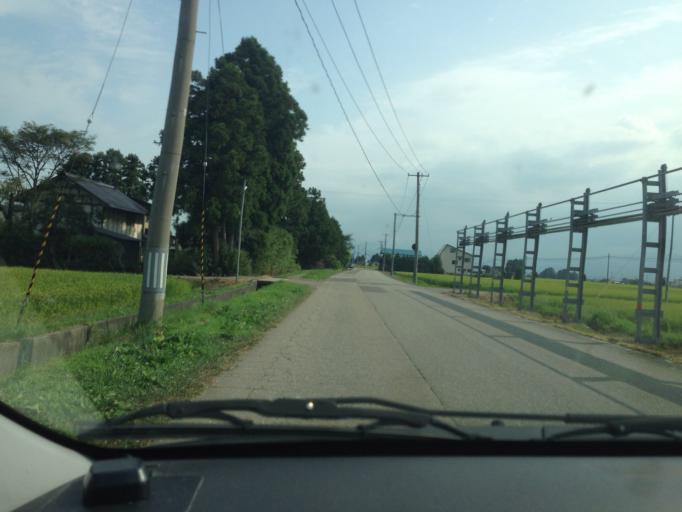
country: JP
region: Fukushima
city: Kitakata
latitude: 37.5732
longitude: 139.8536
